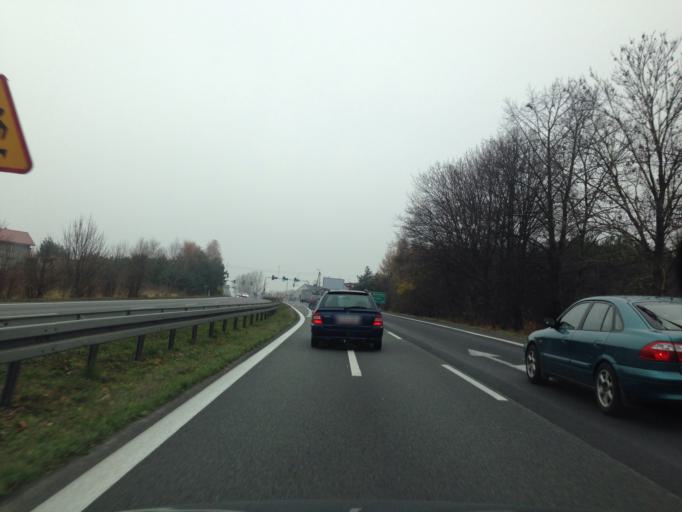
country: PL
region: Silesian Voivodeship
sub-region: Powiat bedzinski
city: Sarnow
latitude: 50.3758
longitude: 19.1493
